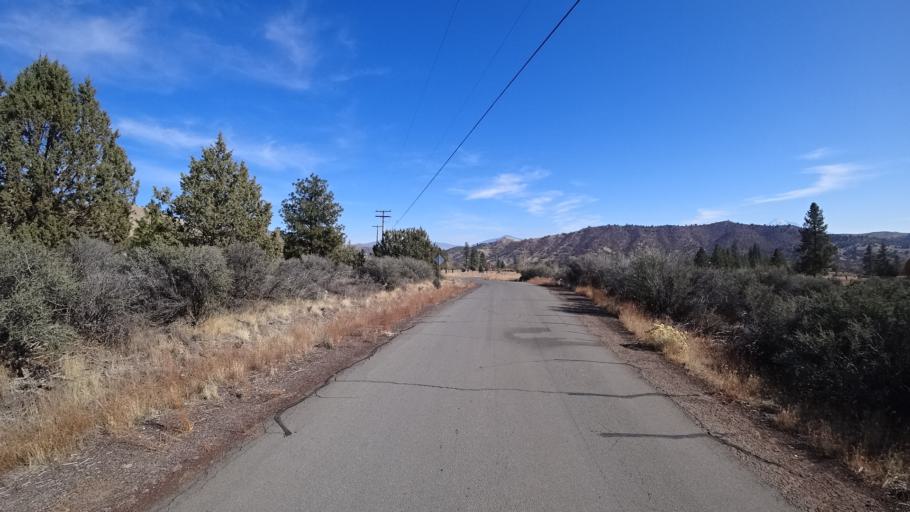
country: US
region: California
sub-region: Siskiyou County
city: Yreka
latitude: 41.7688
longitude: -122.6328
